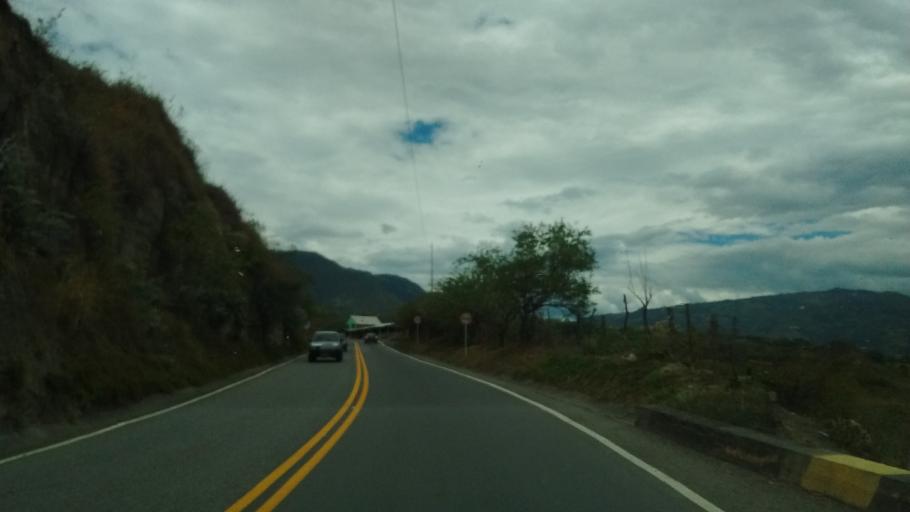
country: CO
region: Cauca
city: La Sierra
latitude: 2.2228
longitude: -76.7958
